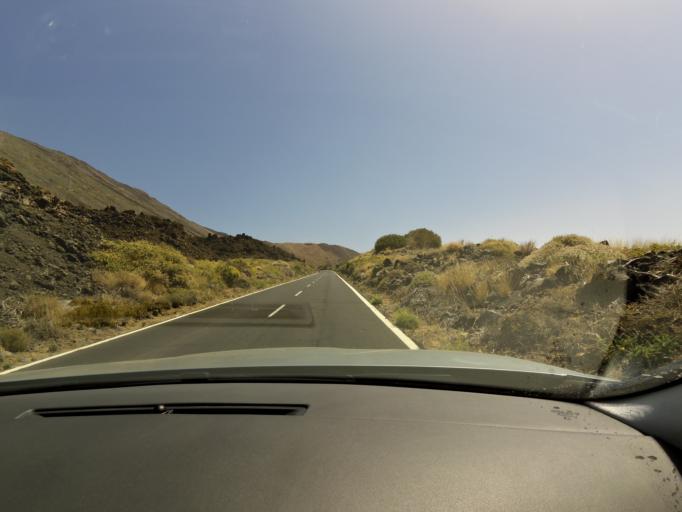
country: ES
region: Canary Islands
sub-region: Provincia de Santa Cruz de Tenerife
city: Vilaflor
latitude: 28.2455
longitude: -16.6289
